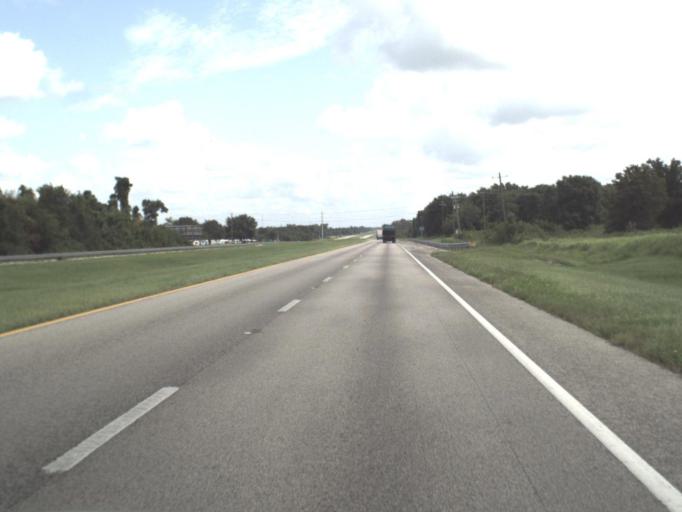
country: US
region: Florida
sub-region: DeSoto County
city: Arcadia
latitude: 27.3050
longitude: -81.8206
